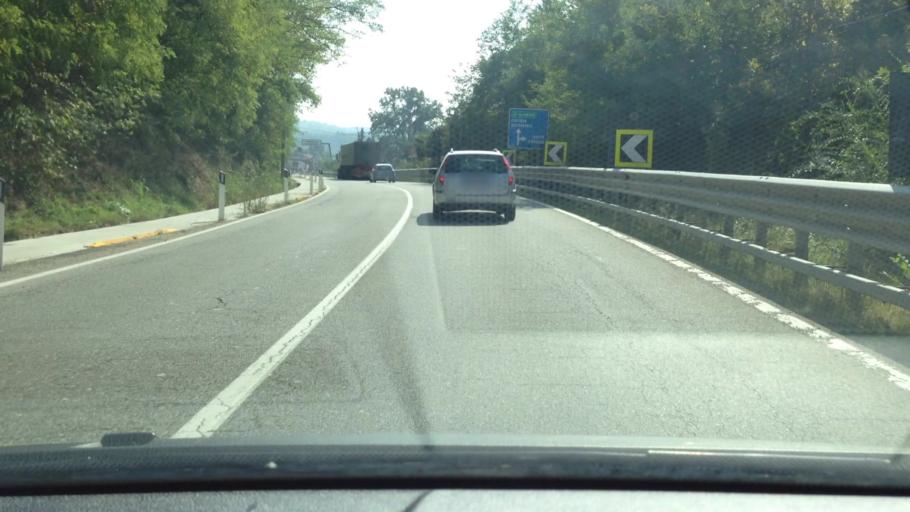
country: IT
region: Piedmont
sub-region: Provincia di Asti
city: Castello di Annone
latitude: 44.8848
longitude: 8.3106
